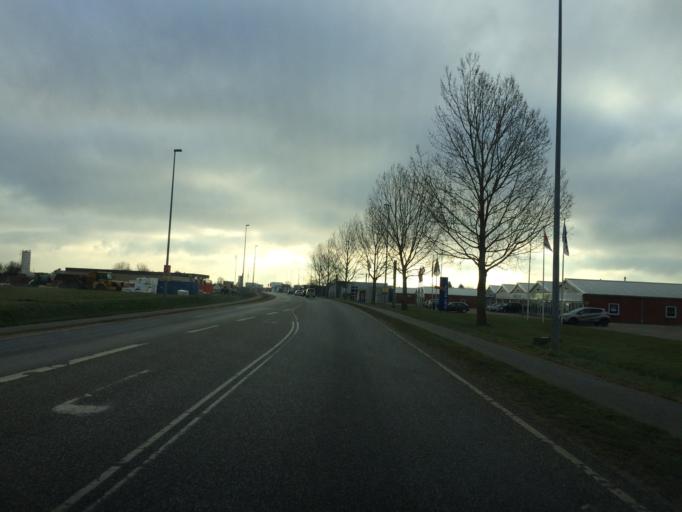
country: DK
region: South Denmark
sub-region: Fredericia Kommune
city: Snoghoj
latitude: 55.5676
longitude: 9.6983
